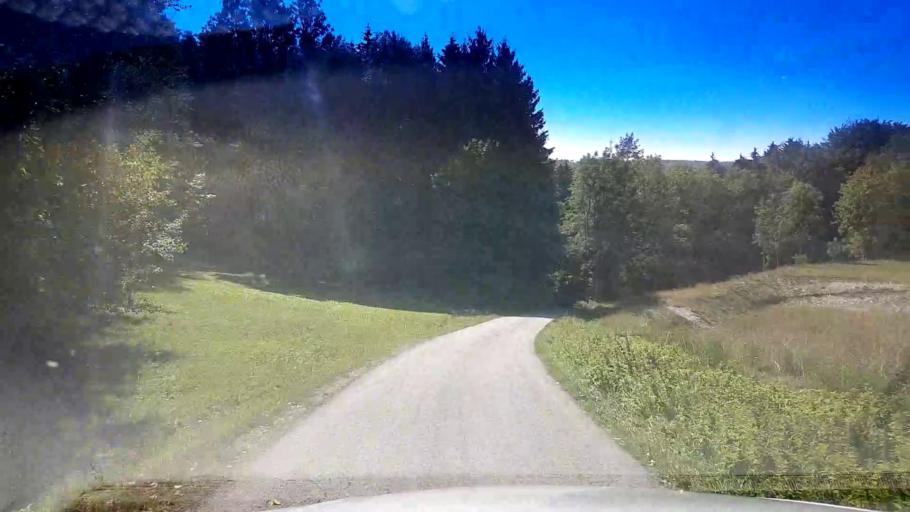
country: DE
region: Bavaria
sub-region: Upper Franconia
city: Poxdorf
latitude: 49.8901
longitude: 11.0839
